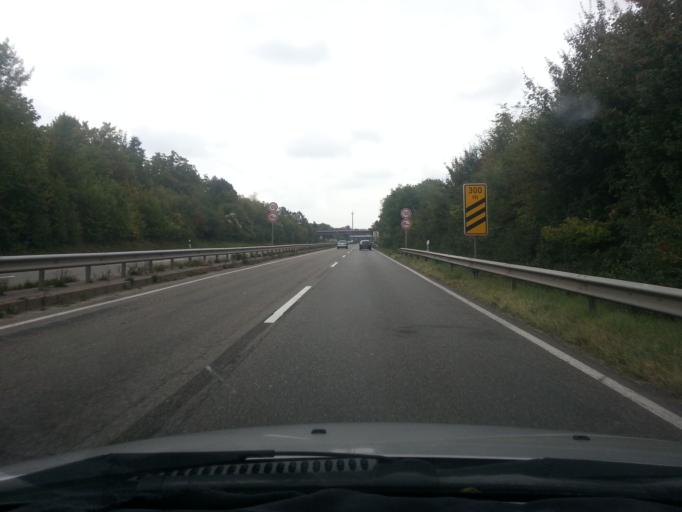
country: DE
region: Rheinland-Pfalz
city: Speyer
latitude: 49.3225
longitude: 8.4104
